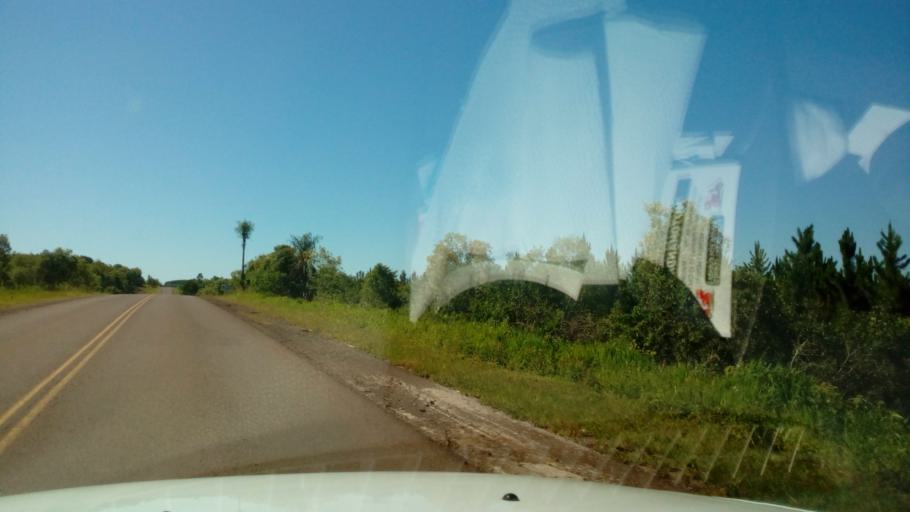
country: AR
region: Misiones
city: Almafuerte
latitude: -27.5433
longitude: -55.4337
